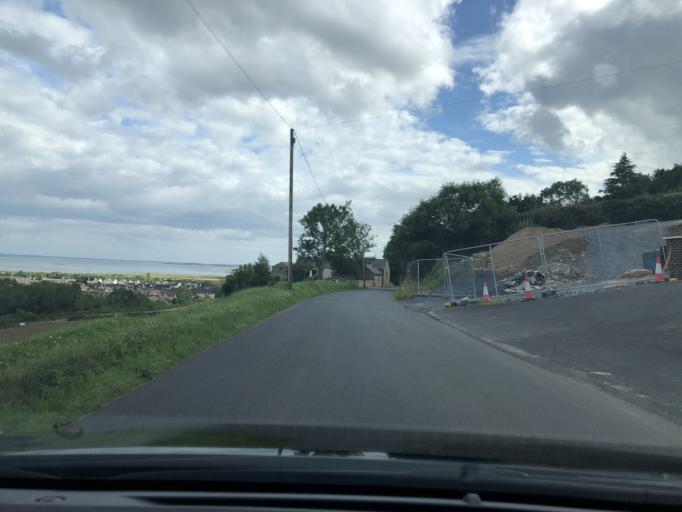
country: GB
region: Northern Ireland
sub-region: Ards District
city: Newtownards
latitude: 54.5808
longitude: -5.7112
